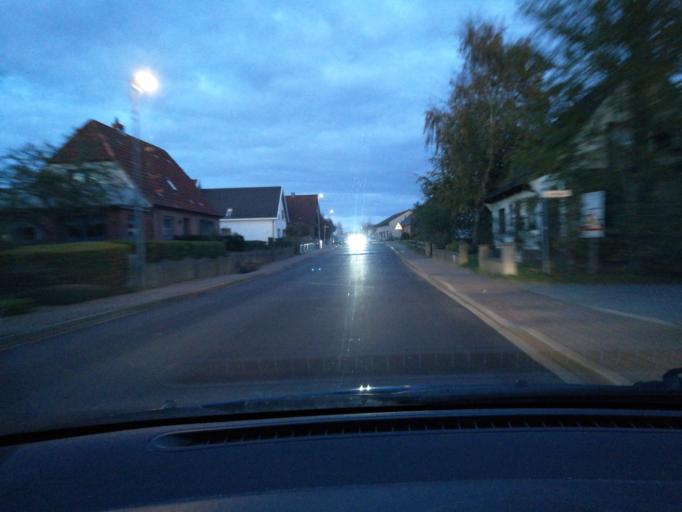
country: DE
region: Schleswig-Holstein
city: Fahrdorf
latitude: 54.5034
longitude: 9.5883
